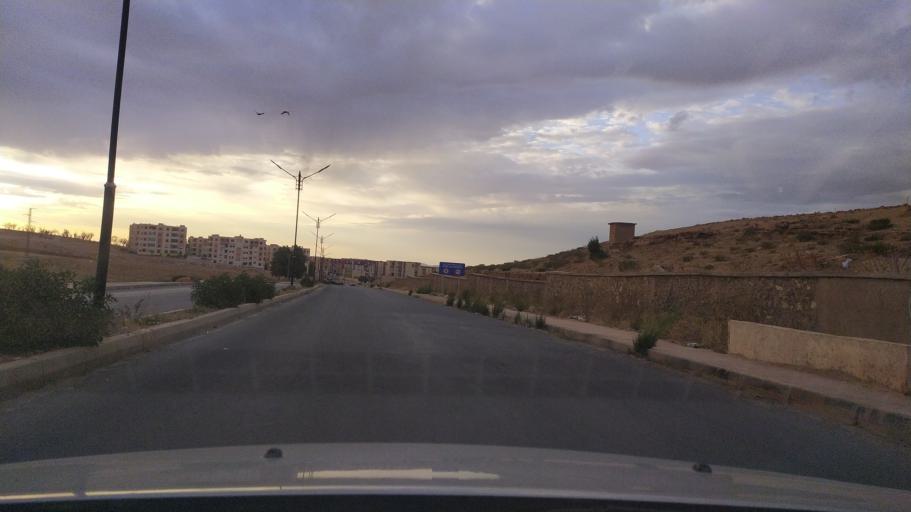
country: DZ
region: Tiaret
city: Frenda
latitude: 35.0525
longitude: 1.0661
